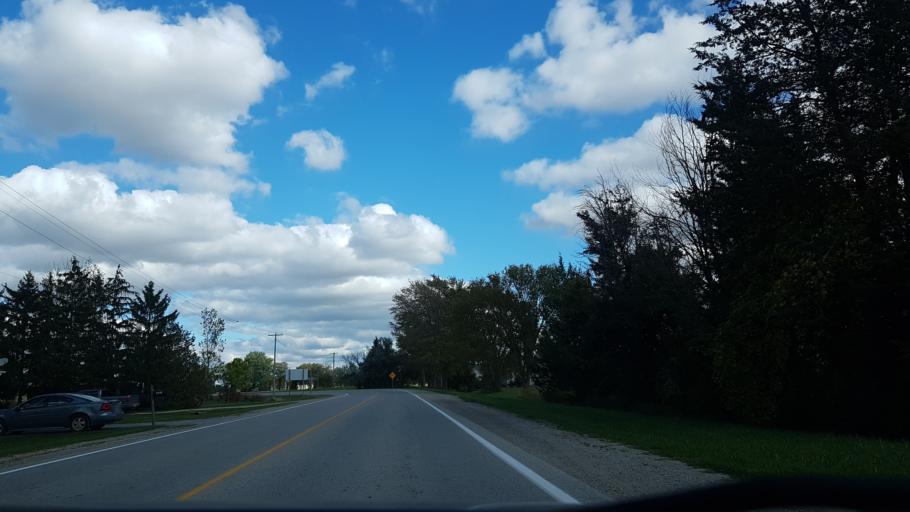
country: CA
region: Ontario
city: South Huron
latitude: 43.2432
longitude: -81.7142
